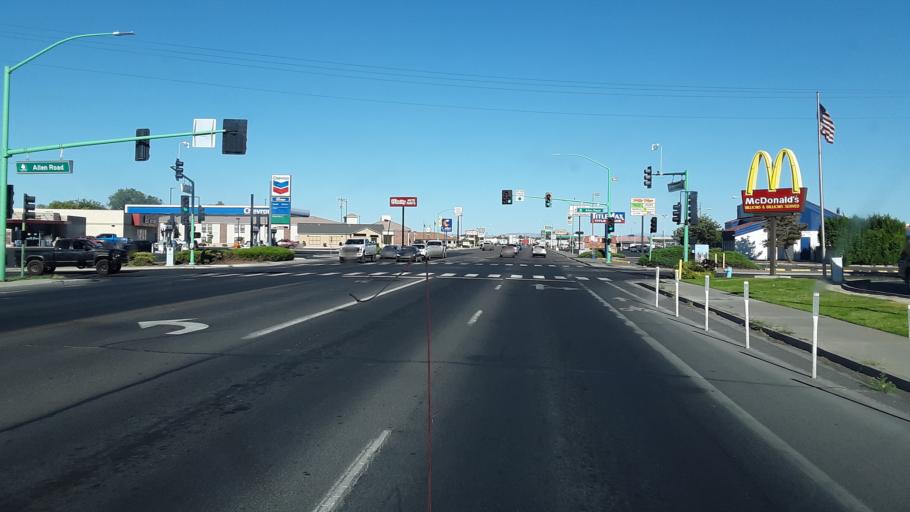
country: US
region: Nevada
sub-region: Churchill County
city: Fallon
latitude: 39.4764
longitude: -118.8009
